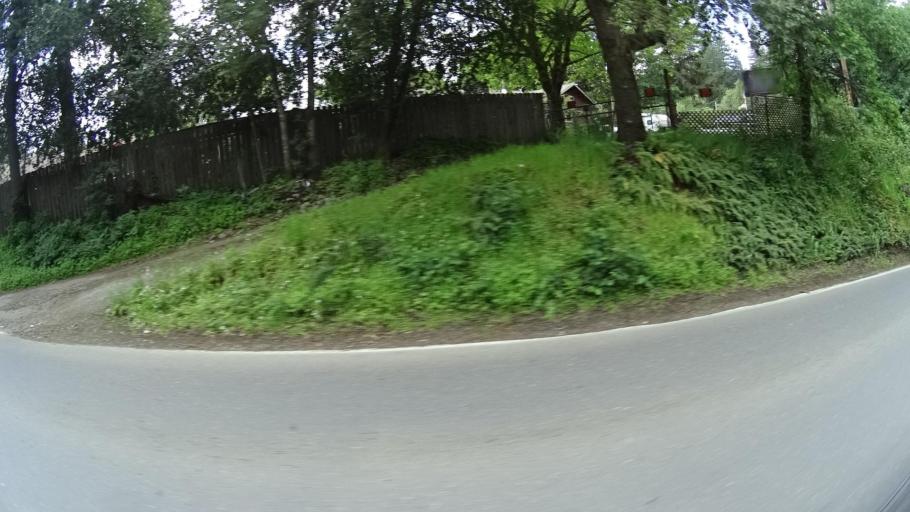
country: US
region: California
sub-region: Humboldt County
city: Redway
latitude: 40.1241
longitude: -123.8308
